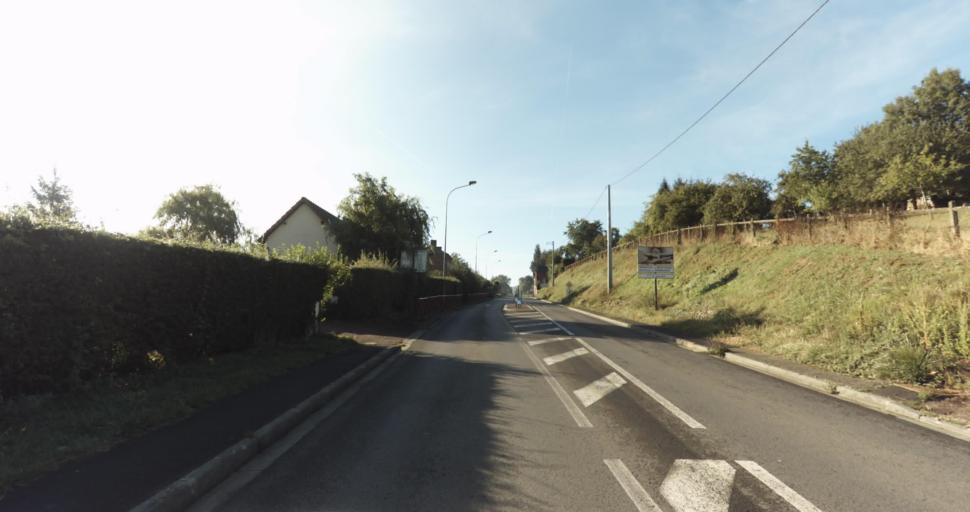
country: FR
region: Lower Normandy
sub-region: Departement de l'Orne
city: Vimoutiers
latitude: 48.9223
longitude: 0.1990
